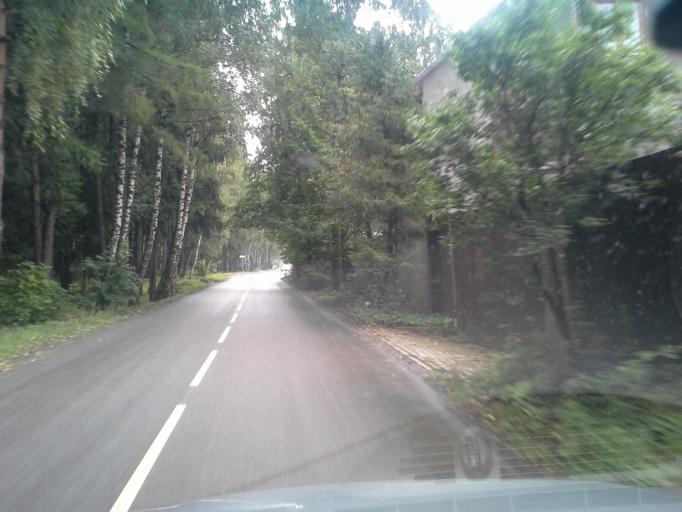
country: RU
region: Moskovskaya
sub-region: Leninskiy Rayon
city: Vnukovo
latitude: 55.6312
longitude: 37.3093
